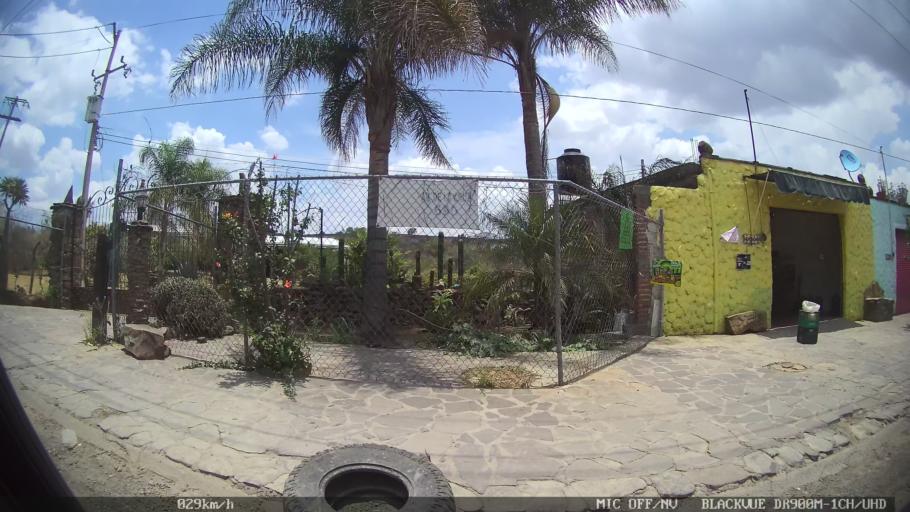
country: MX
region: Jalisco
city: Tonala
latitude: 20.6394
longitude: -103.2226
